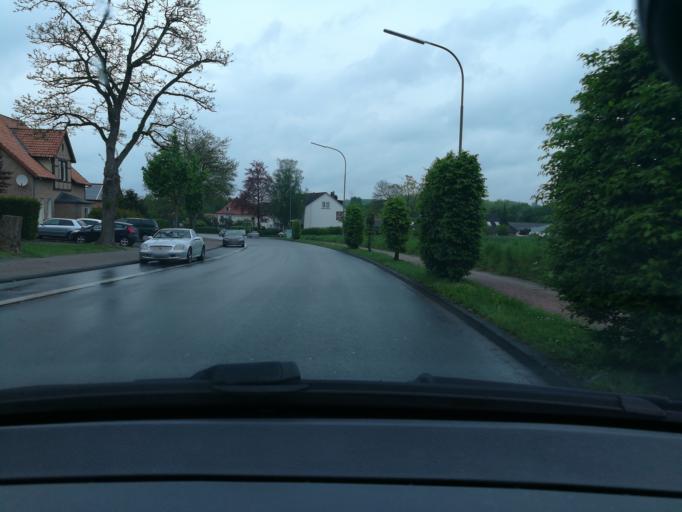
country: DE
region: North Rhine-Westphalia
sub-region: Regierungsbezirk Detmold
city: Herford
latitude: 52.1008
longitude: 8.6823
